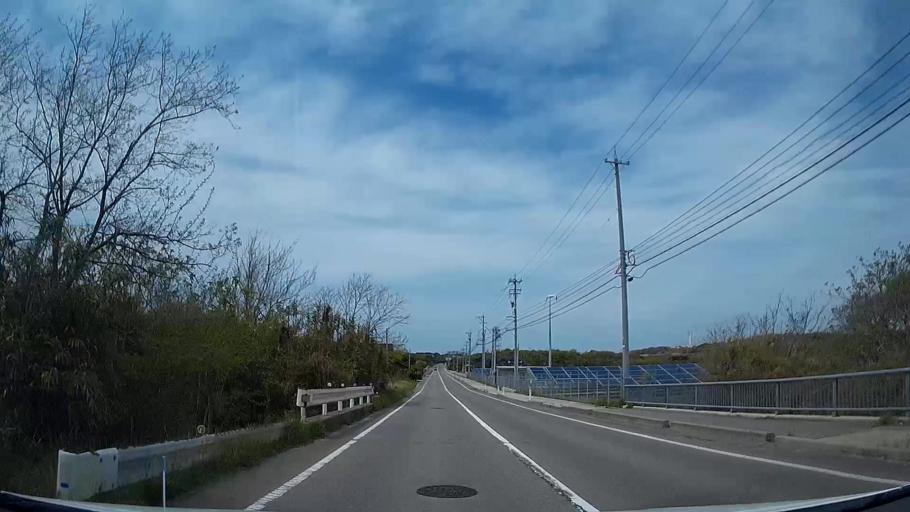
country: JP
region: Ishikawa
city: Hakui
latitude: 36.9810
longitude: 136.7764
